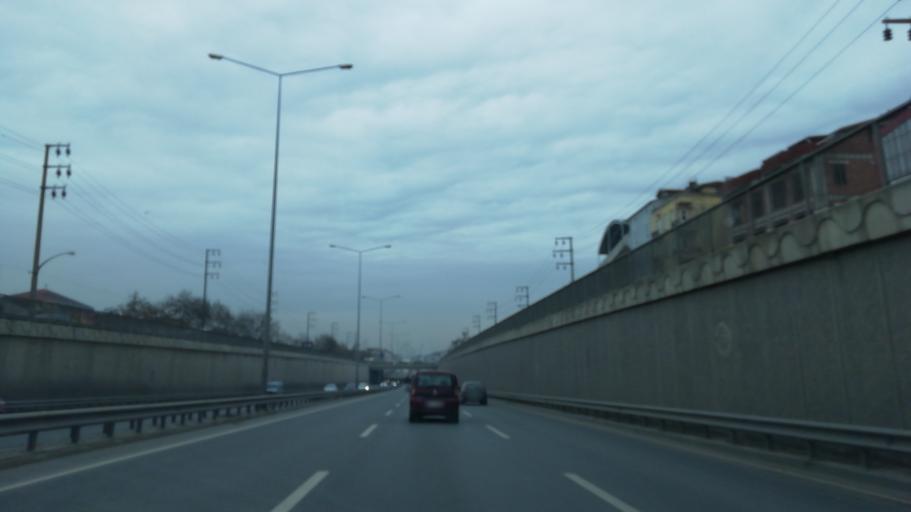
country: TR
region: Kocaeli
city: Derince
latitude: 40.7564
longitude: 29.8164
